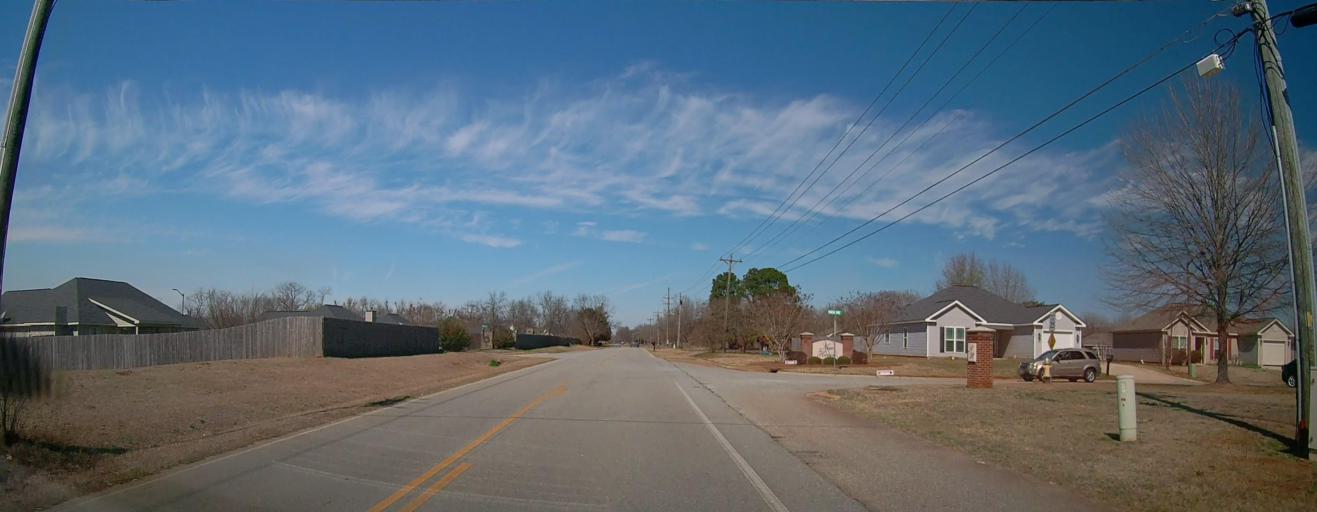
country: US
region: Georgia
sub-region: Houston County
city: Perry
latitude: 32.4582
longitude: -83.6827
